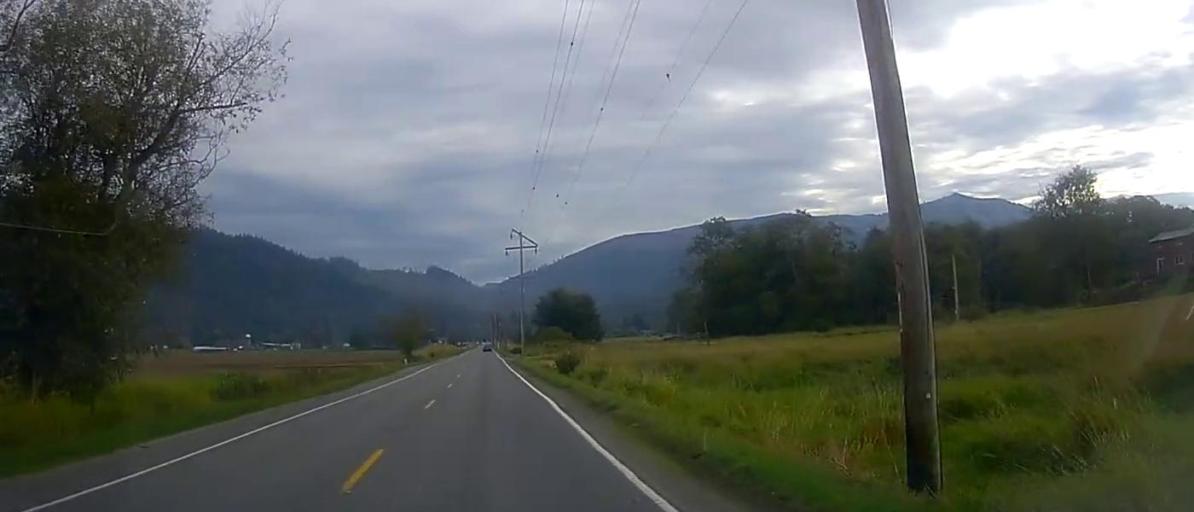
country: US
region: Washington
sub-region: Skagit County
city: Clear Lake
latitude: 48.4679
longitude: -122.2437
